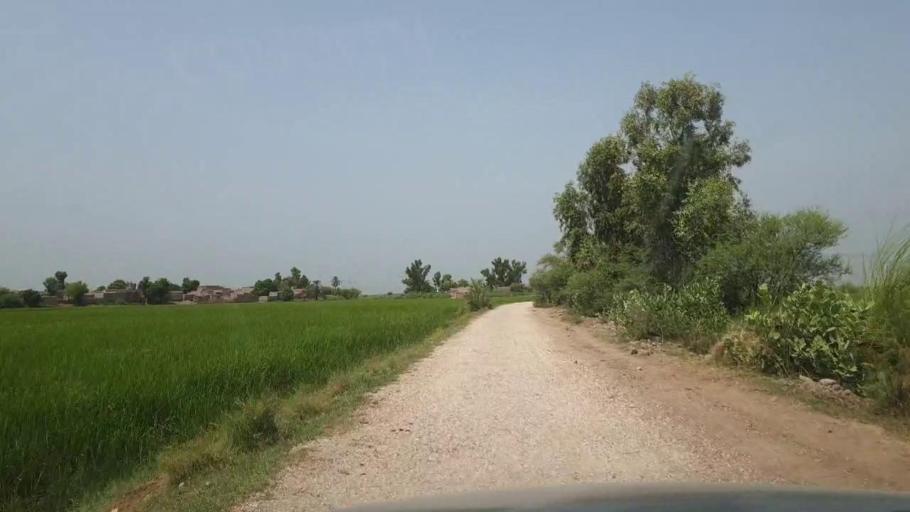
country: PK
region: Sindh
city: Madeji
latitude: 27.8126
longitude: 68.5211
